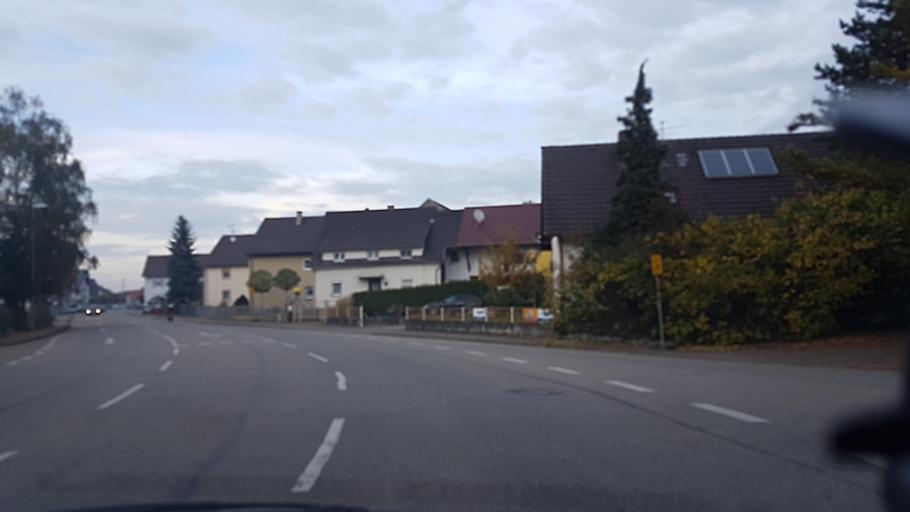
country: DE
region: Baden-Wuerttemberg
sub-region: Freiburg Region
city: Weisweil
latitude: 48.2222
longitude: 7.7104
